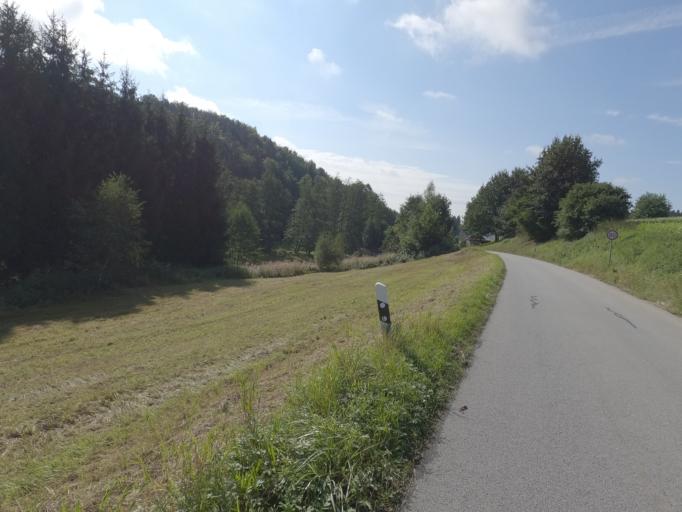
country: DE
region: Bavaria
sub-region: Lower Bavaria
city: Niederalteich
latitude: 48.8090
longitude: 13.0092
